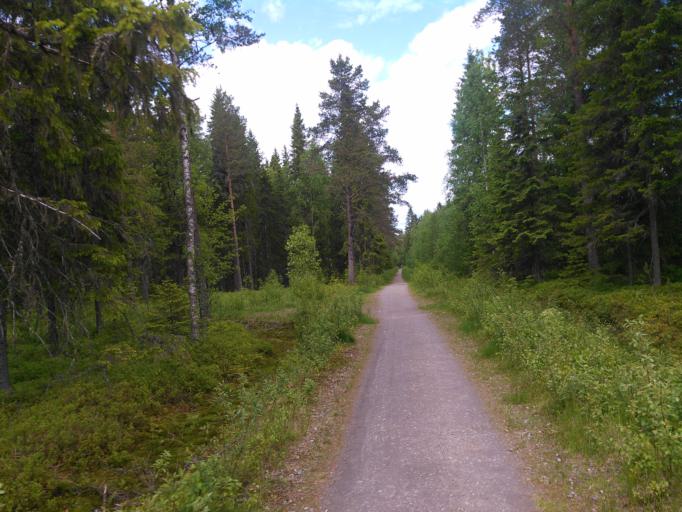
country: SE
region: Vaesterbotten
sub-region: Umea Kommun
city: Ersmark
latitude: 63.8667
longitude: 20.3338
